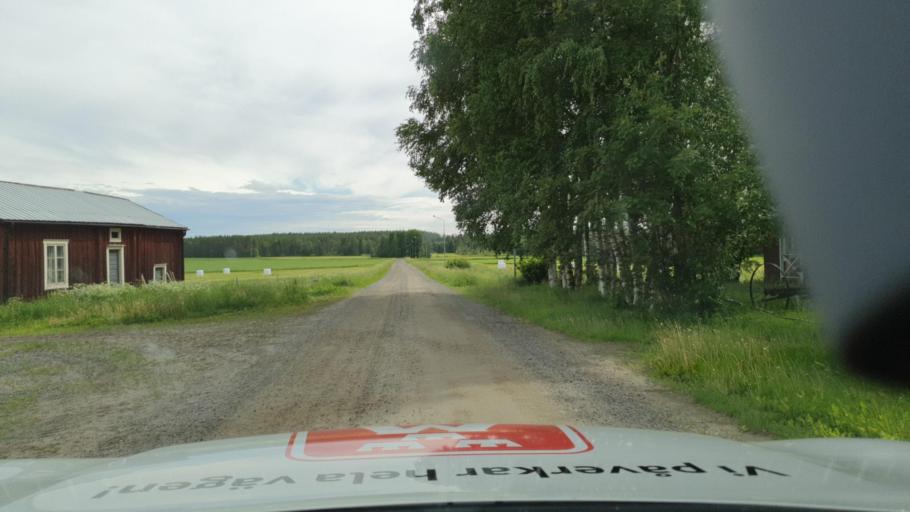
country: SE
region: Vaesterbotten
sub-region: Robertsfors Kommun
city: Robertsfors
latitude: 64.3817
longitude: 21.0355
